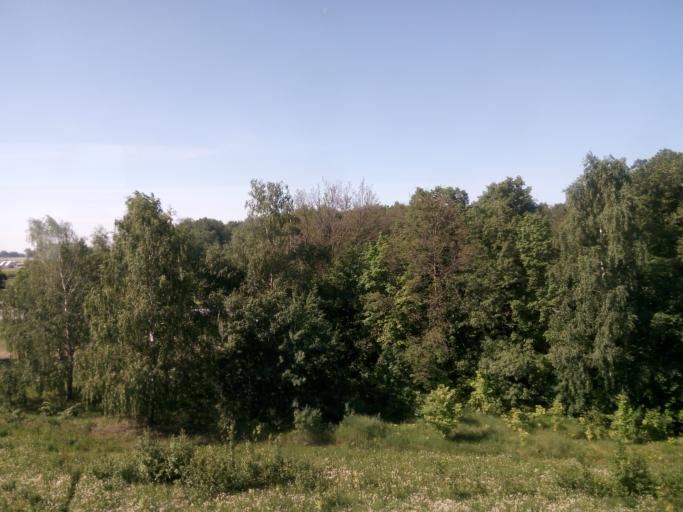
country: RU
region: Tatarstan
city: Stolbishchi
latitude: 55.6124
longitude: 49.2915
